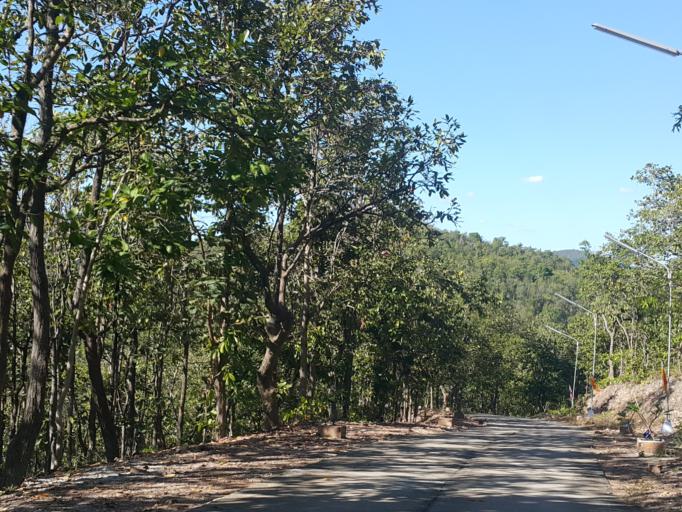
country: TH
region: Chiang Mai
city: San Sai
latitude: 18.9150
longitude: 99.1203
